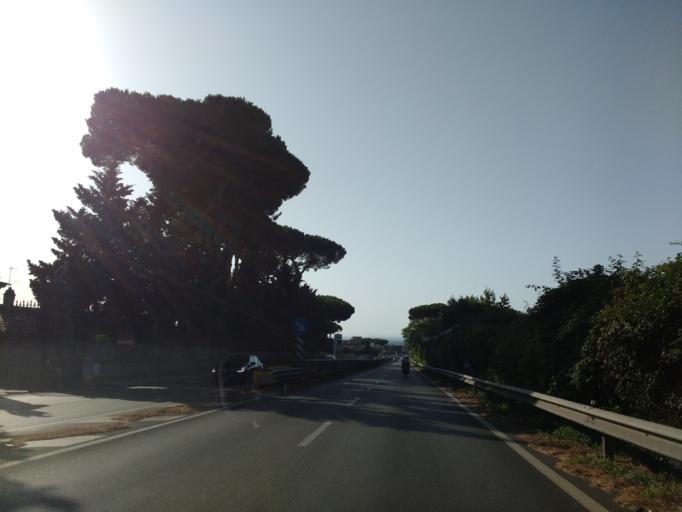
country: IT
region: Latium
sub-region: Citta metropolitana di Roma Capitale
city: Marino
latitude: 41.7568
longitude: 12.6275
